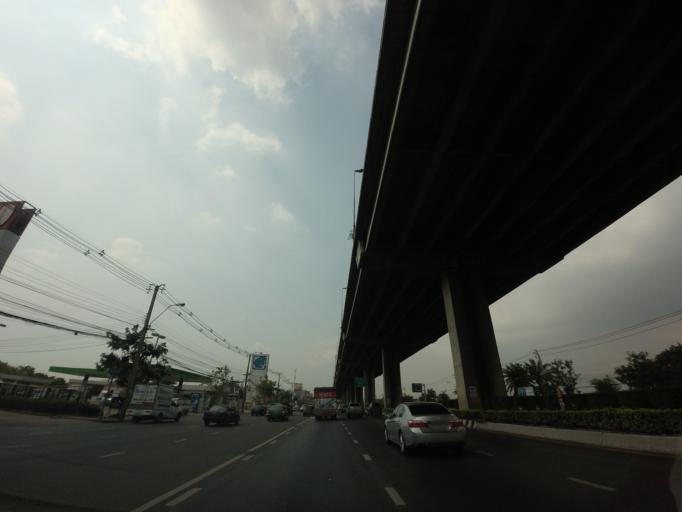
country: TH
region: Bangkok
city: Taling Chan
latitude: 13.7839
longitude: 100.3987
